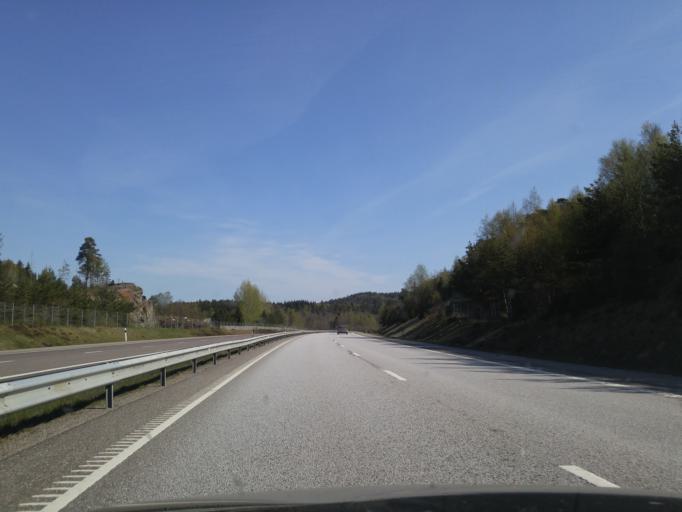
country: SE
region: Vaestra Goetaland
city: Svanesund
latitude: 58.1628
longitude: 11.8885
